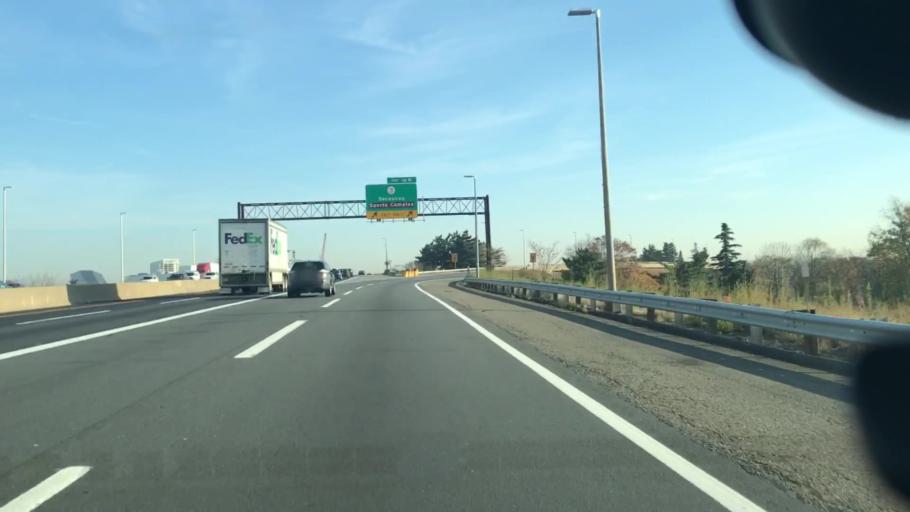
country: US
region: New Jersey
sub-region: Hudson County
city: Secaucus
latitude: 40.7980
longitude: -74.0779
